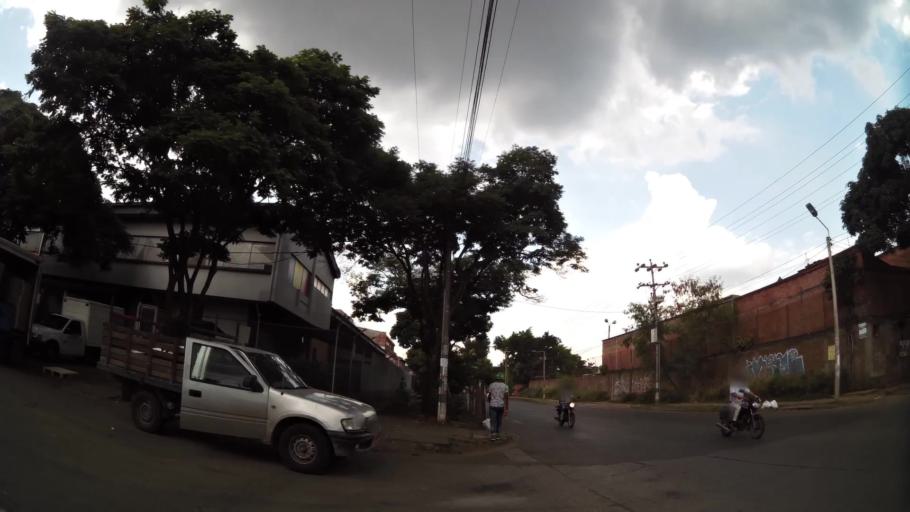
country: CO
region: Valle del Cauca
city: Cali
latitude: 3.4808
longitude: -76.5041
